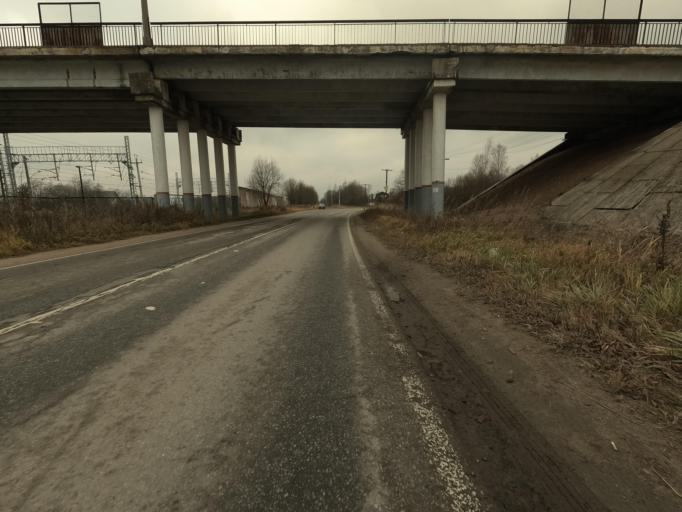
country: RU
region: Leningrad
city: Lyuban'
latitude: 59.4883
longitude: 31.2677
